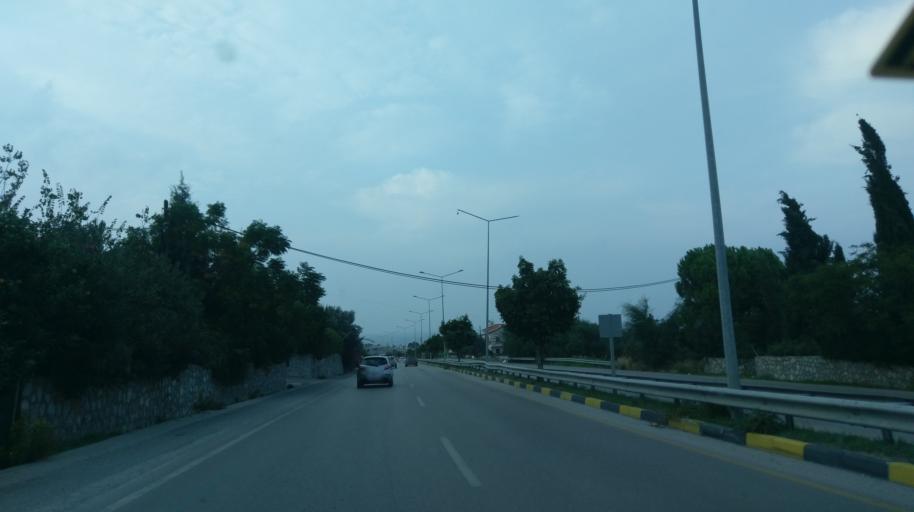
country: CY
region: Keryneia
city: Kyrenia
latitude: 35.3368
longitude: 33.2573
